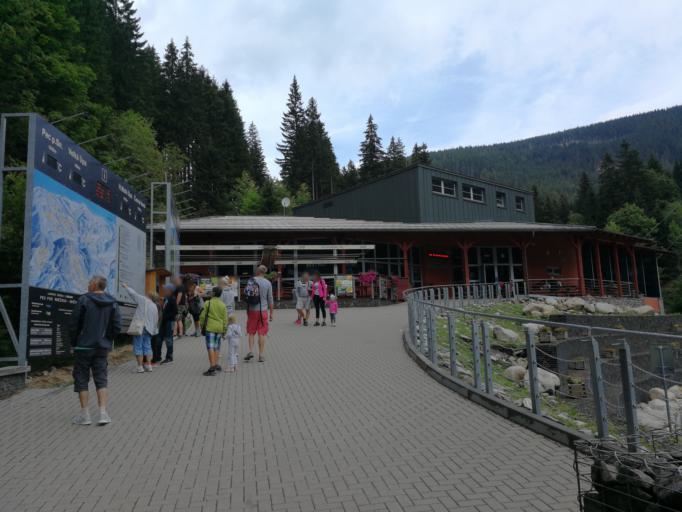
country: PL
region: Lower Silesian Voivodeship
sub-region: Powiat jeleniogorski
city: Karpacz
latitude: 50.7045
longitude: 15.7330
